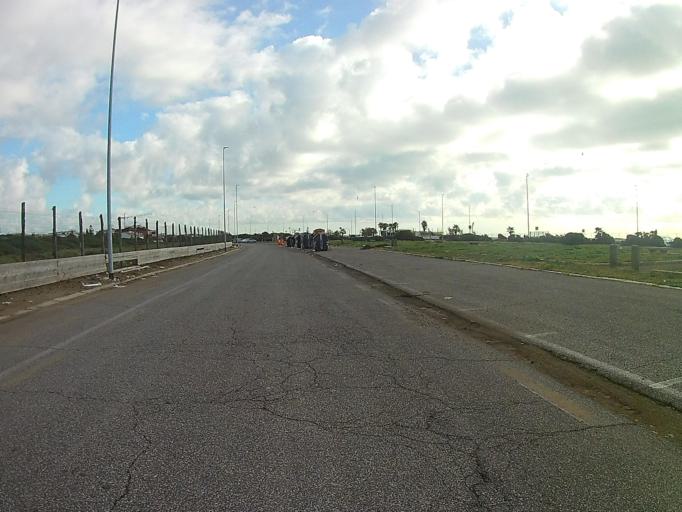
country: IT
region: Latium
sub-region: Citta metropolitana di Roma Capitale
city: Lido di Ostia
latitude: 41.7179
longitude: 12.3081
